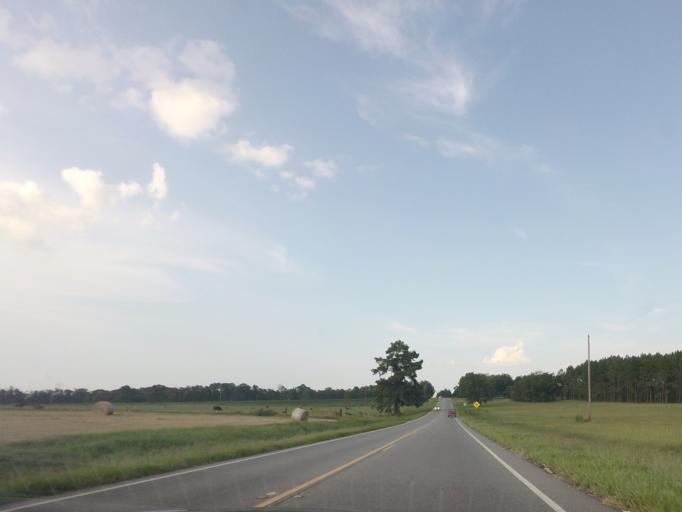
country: US
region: Georgia
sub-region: Bleckley County
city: Cochran
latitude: 32.4176
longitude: -83.3174
